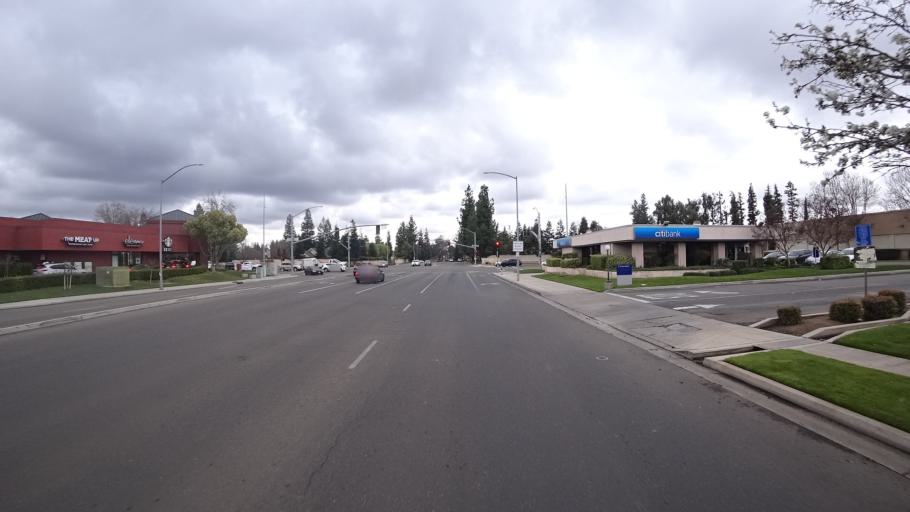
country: US
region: California
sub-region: Fresno County
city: Fresno
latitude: 36.8379
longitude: -119.8476
